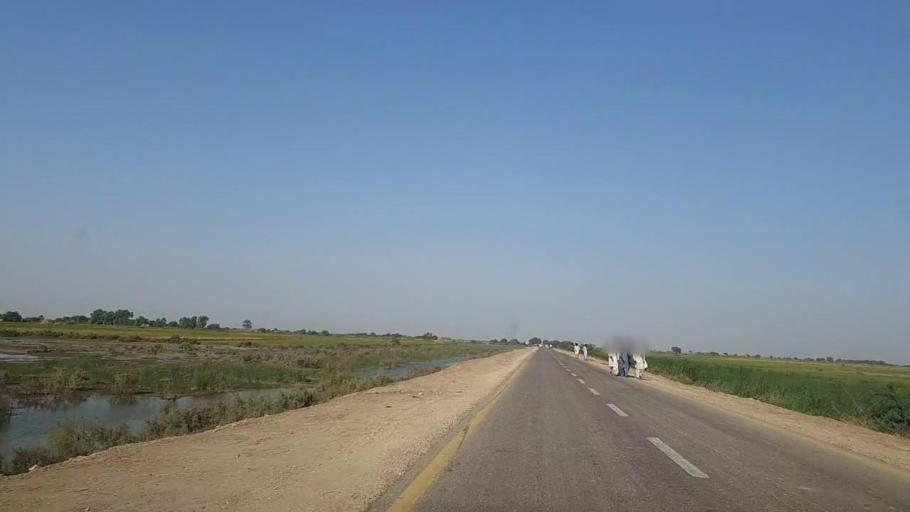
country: PK
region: Sindh
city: Jati
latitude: 24.4086
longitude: 68.2984
